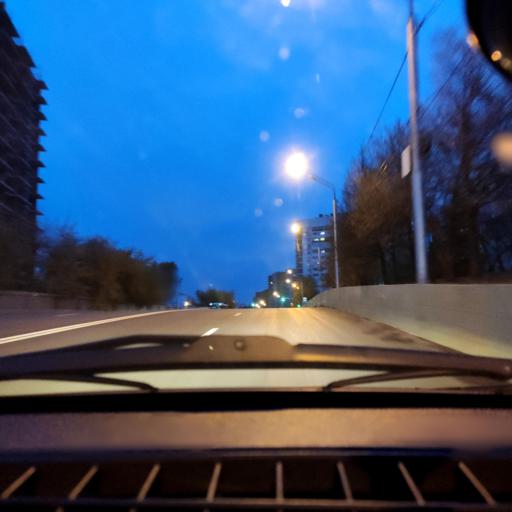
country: RU
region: Bashkortostan
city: Ufa
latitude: 54.7002
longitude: 55.9803
